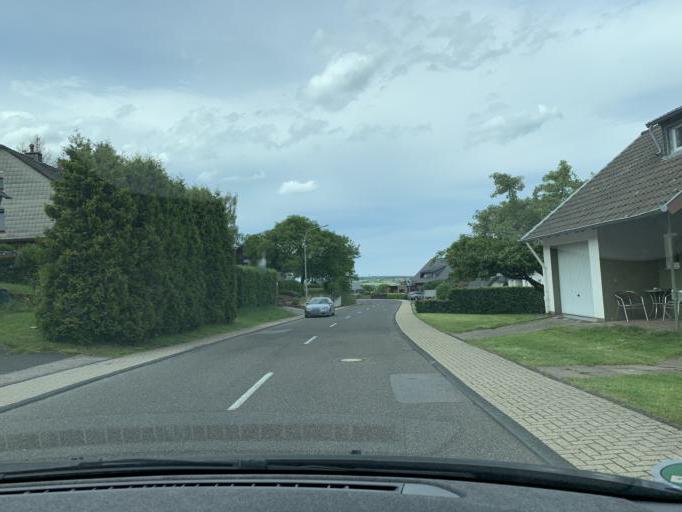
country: DE
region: North Rhine-Westphalia
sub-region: Regierungsbezirk Koln
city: Hurtgenwald
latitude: 50.6692
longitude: 6.4101
